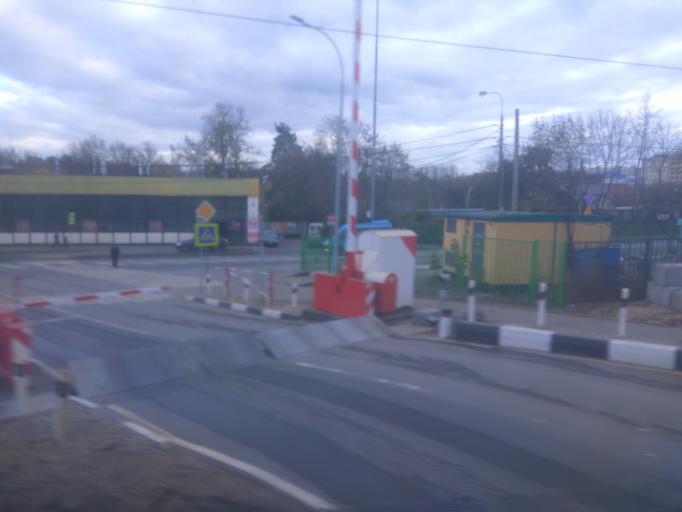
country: RU
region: Moscow
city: Novo-Peredelkino
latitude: 55.6561
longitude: 37.3519
